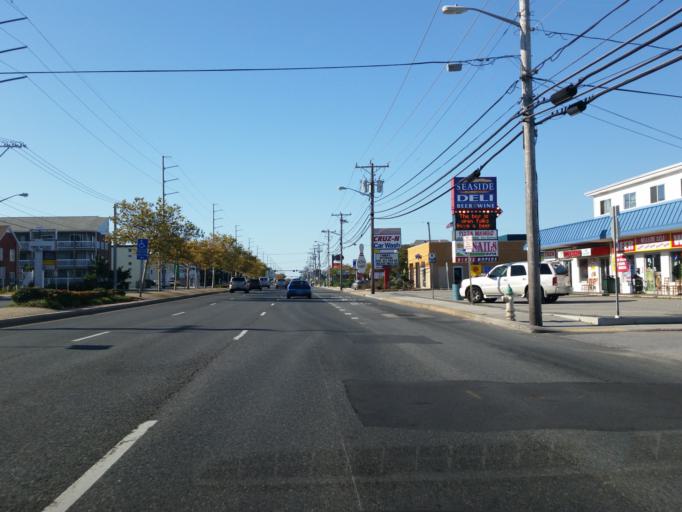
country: US
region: Maryland
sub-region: Worcester County
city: Ocean City
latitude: 38.3939
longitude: -75.0636
